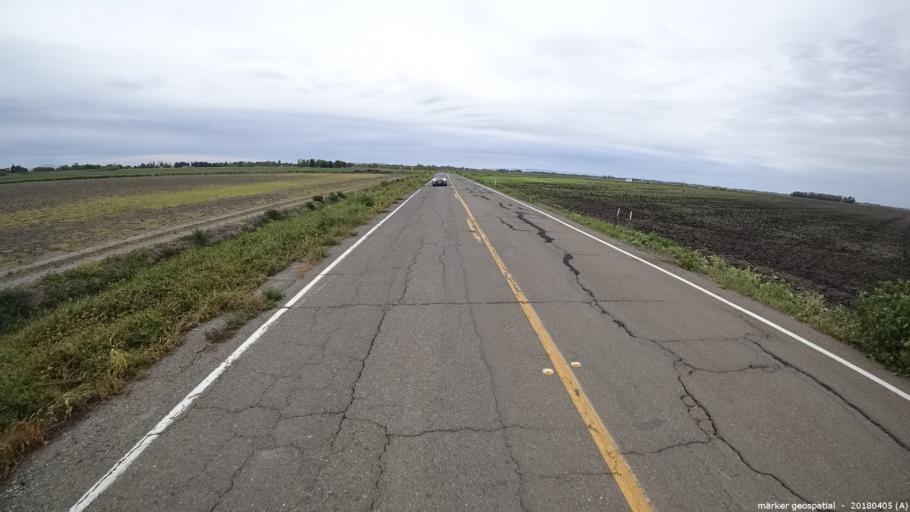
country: US
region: California
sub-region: Sacramento County
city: Walnut Grove
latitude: 38.2844
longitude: -121.5232
